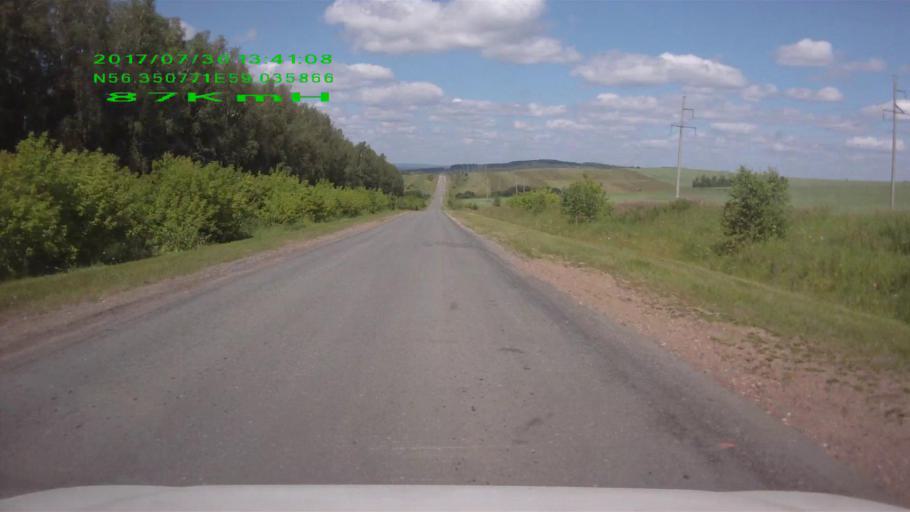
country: RU
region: Sverdlovsk
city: Mikhaylovsk
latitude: 56.3513
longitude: 59.0359
